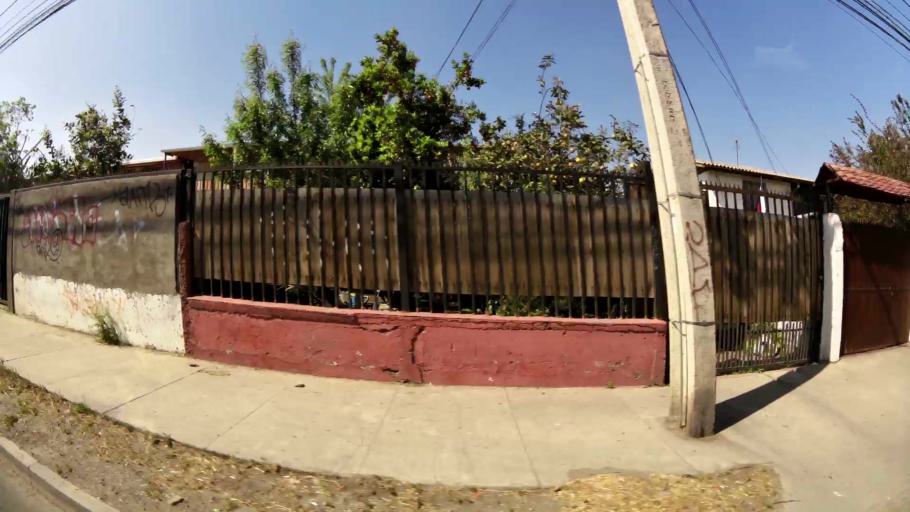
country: CL
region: Santiago Metropolitan
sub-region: Provincia de Santiago
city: Lo Prado
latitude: -33.4125
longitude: -70.6922
